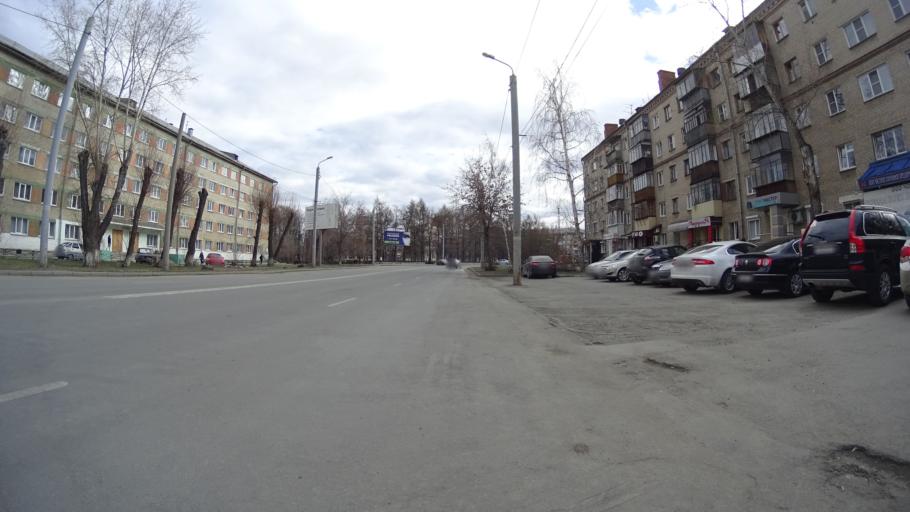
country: RU
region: Chelyabinsk
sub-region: Gorod Chelyabinsk
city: Chelyabinsk
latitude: 55.1497
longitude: 61.3803
